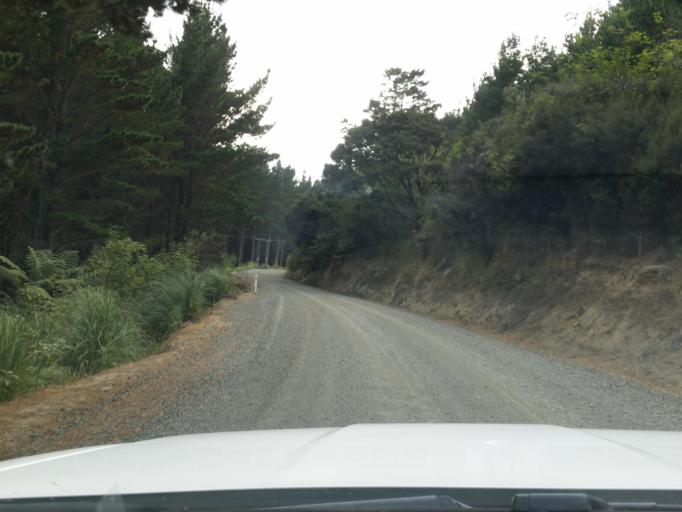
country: NZ
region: Northland
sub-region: Kaipara District
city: Dargaville
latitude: -36.2367
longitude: 174.0647
